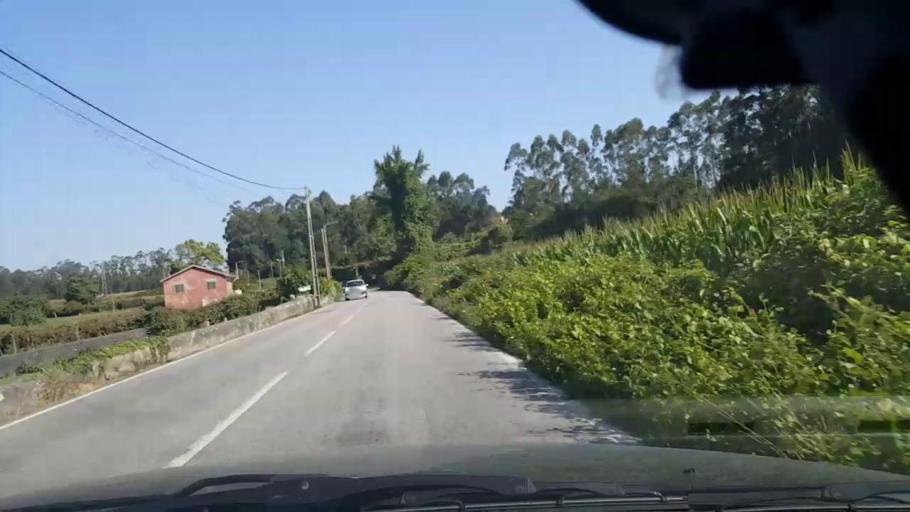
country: PT
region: Porto
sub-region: Vila do Conde
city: Arvore
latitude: 41.3144
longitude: -8.6790
